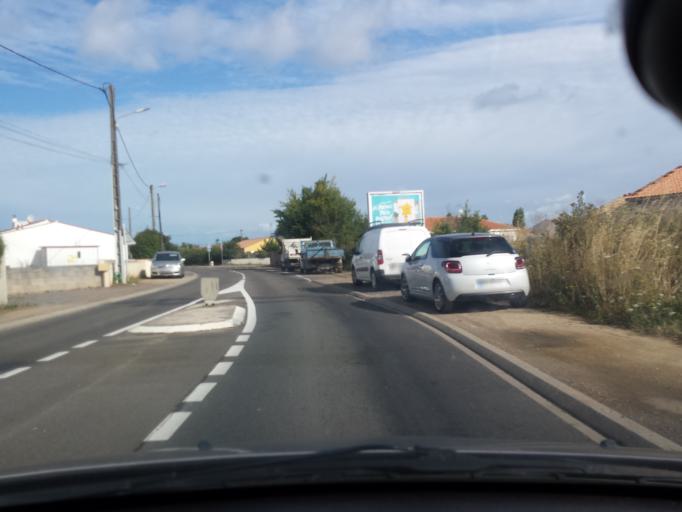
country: FR
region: Pays de la Loire
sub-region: Departement de la Vendee
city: Olonne-sur-Mer
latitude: 46.5413
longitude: -1.7958
